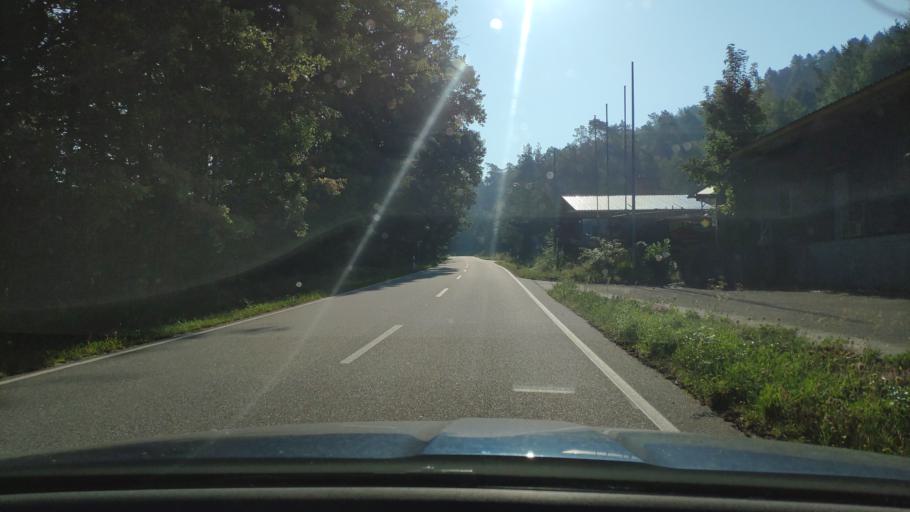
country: DE
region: Rheinland-Pfalz
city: Fischbach
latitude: 49.0699
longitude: 7.6932
